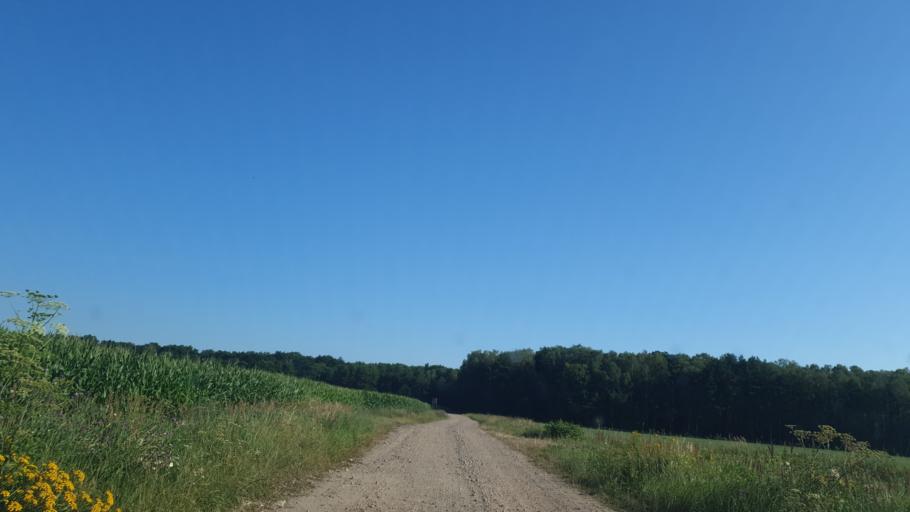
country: DE
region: Mecklenburg-Vorpommern
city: Torgelow
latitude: 53.6501
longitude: 13.9516
